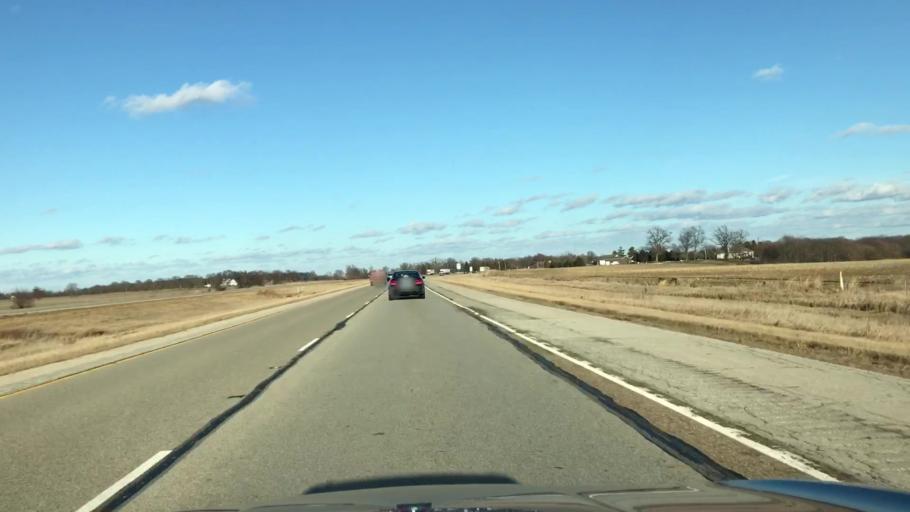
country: US
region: Illinois
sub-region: McLean County
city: Hudson
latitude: 40.5761
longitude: -88.8960
